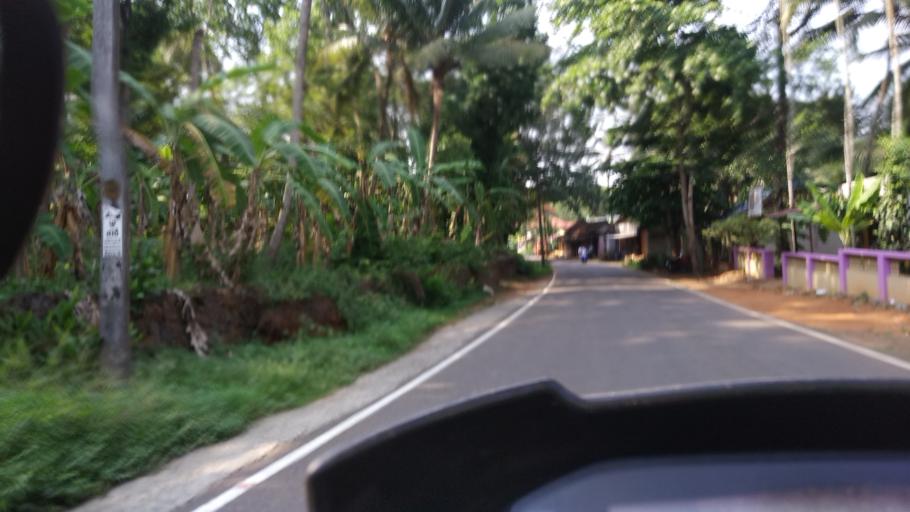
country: IN
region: Kerala
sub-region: Ernakulam
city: Piravam
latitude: 9.8211
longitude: 76.5518
